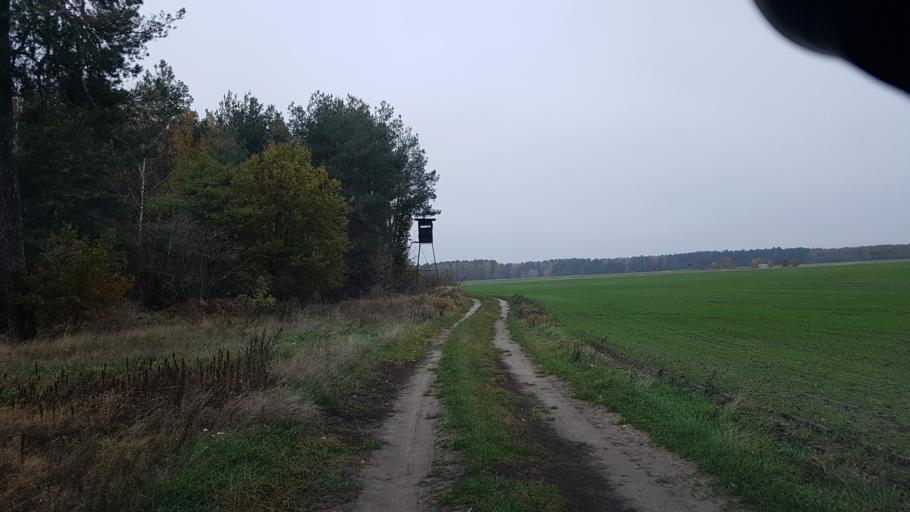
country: DE
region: Brandenburg
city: Ruckersdorf
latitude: 51.5682
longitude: 13.6462
